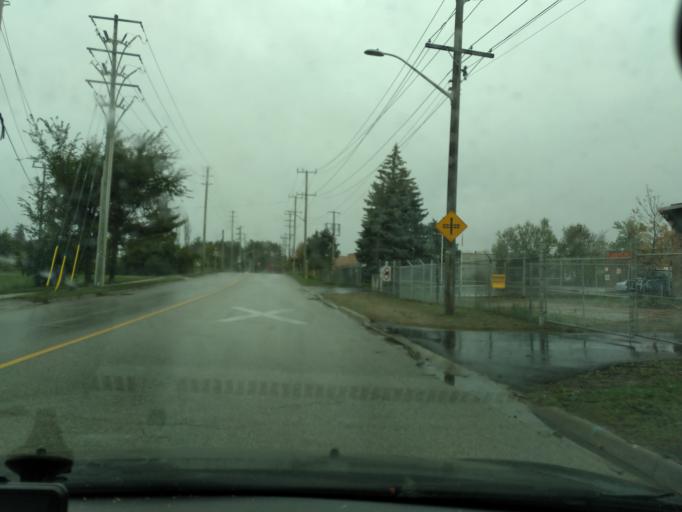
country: CA
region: Ontario
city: Barrie
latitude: 44.3679
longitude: -79.7083
